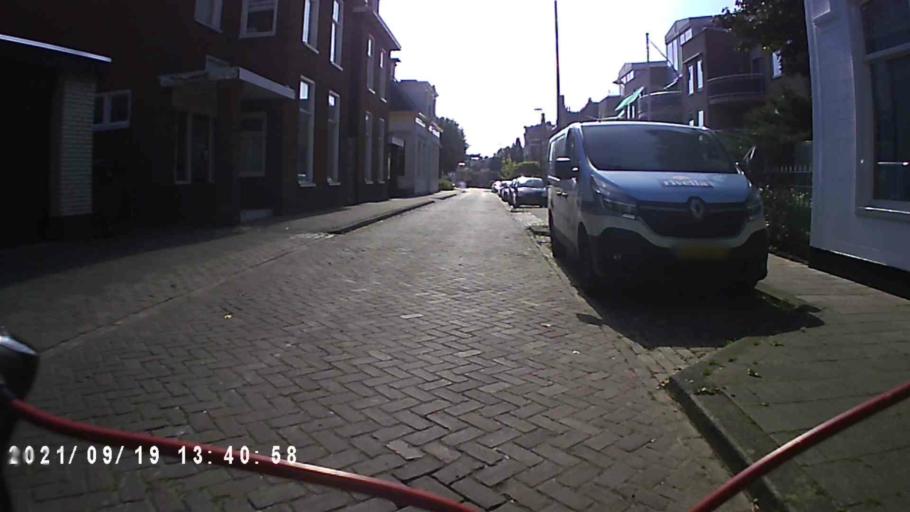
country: NL
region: Groningen
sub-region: Gemeente  Oldambt
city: Winschoten
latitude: 53.1404
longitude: 7.0398
